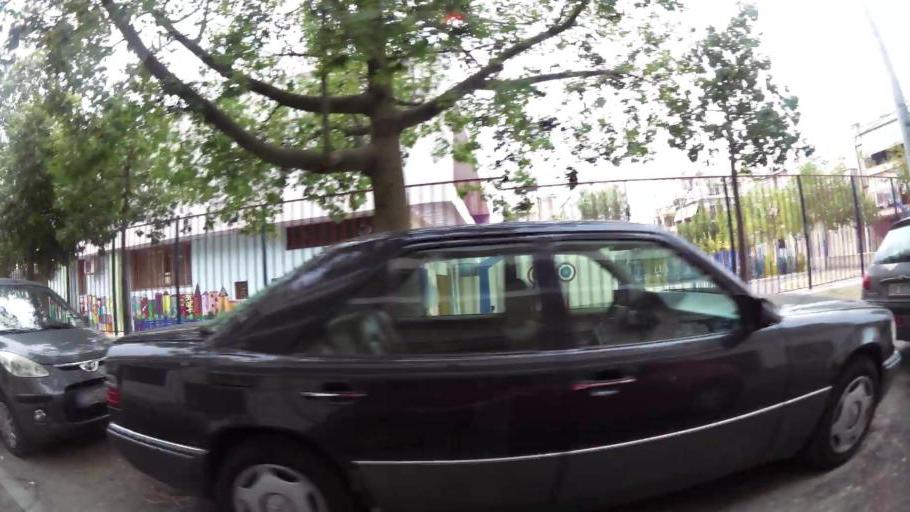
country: GR
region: Attica
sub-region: Nomarchia Athinas
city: Agioi Anargyroi
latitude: 38.0320
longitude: 23.7154
